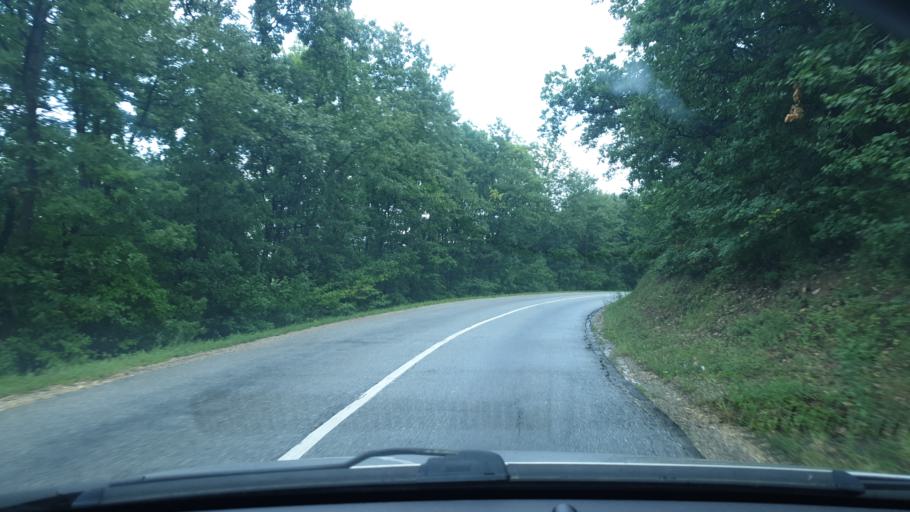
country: RS
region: Central Serbia
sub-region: Sumadijski Okrug
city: Kragujevac
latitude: 44.0481
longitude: 20.7864
